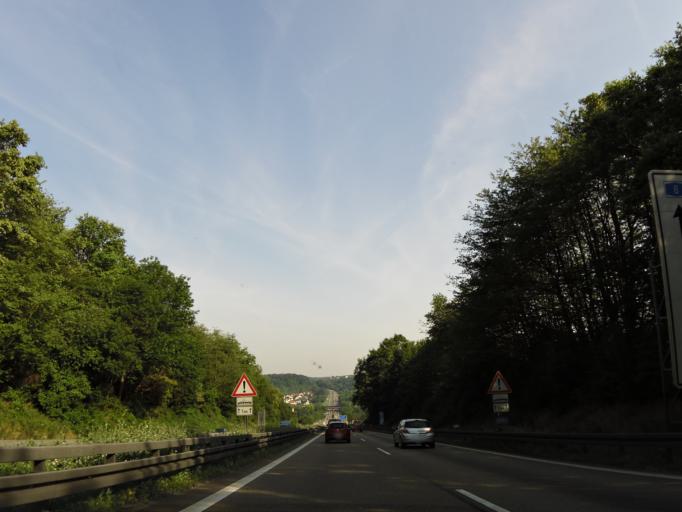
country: DE
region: Baden-Wuerttemberg
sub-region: Karlsruhe Region
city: Niefern-Oschelbronn
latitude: 48.9106
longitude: 8.7693
